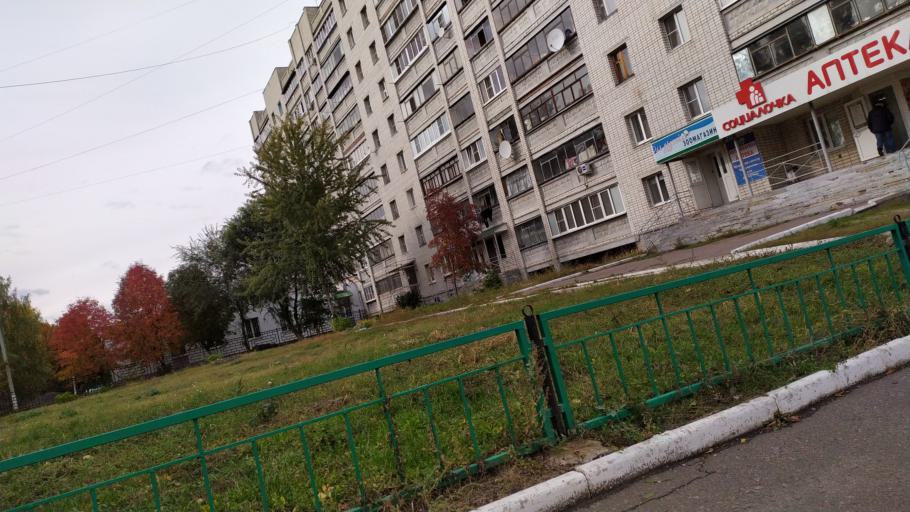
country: RU
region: Kursk
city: Kursk
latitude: 51.6492
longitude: 36.1462
